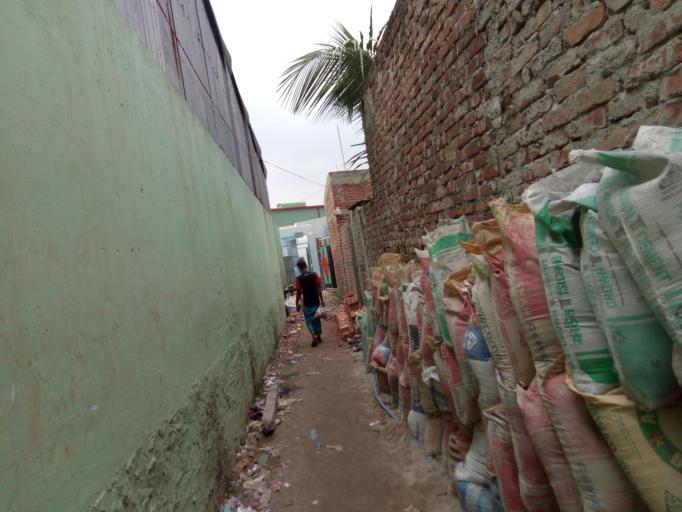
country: BD
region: Dhaka
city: Paltan
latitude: 23.7535
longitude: 90.4517
